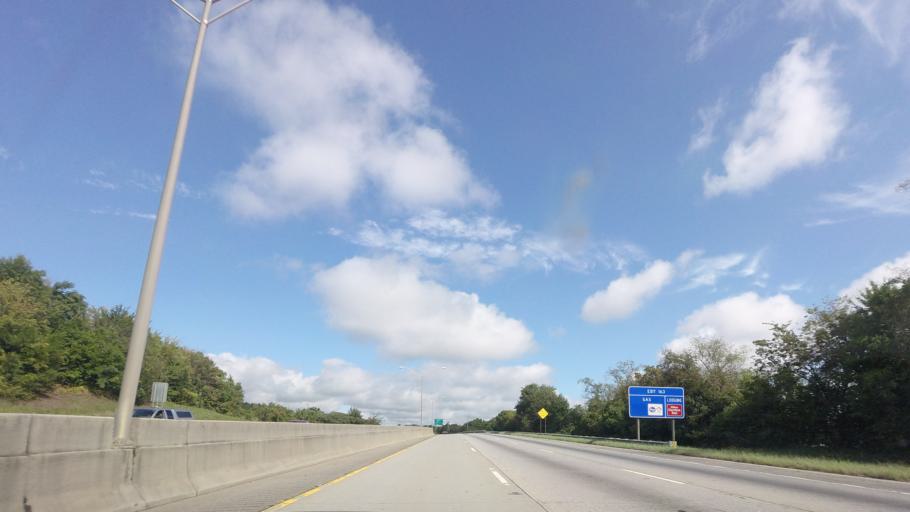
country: US
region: Georgia
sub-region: Bibb County
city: Macon
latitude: 32.8187
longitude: -83.6556
